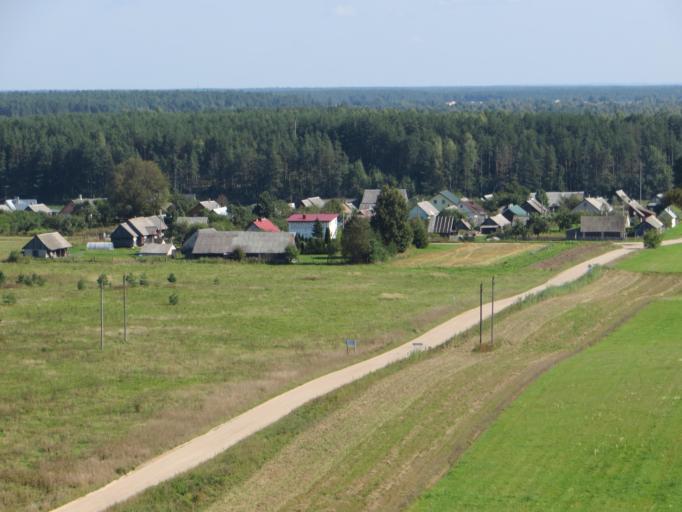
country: LT
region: Vilnius County
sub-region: Trakai
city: Rudiskes
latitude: 54.4604
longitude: 24.9667
